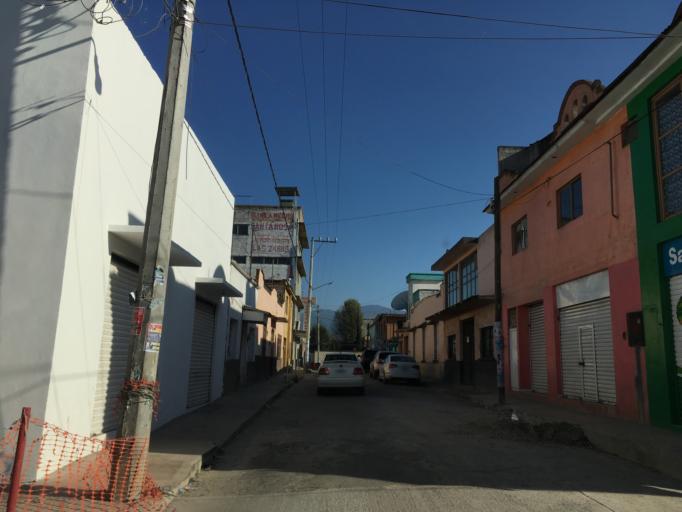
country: MX
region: Michoacan
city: Heroica Zitacuaro
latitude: 19.4380
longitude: -100.3547
